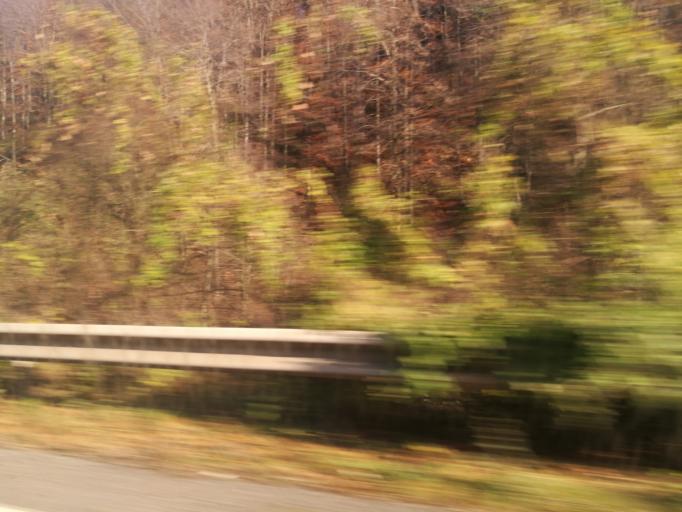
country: RO
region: Brasov
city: Brasov
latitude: 45.5788
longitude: 25.6198
